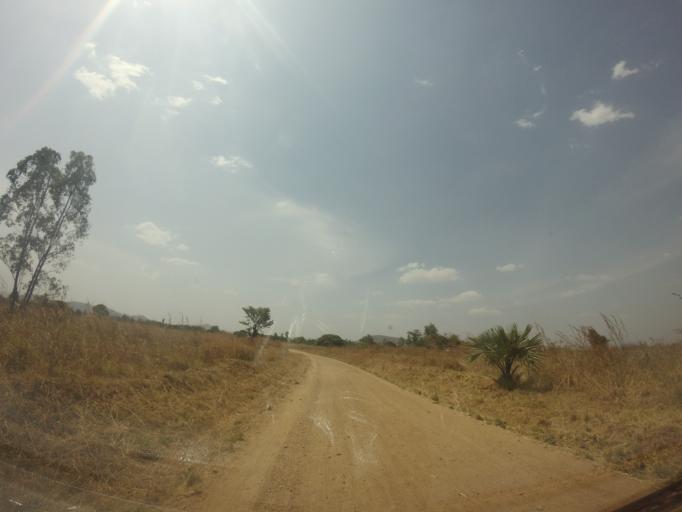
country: UG
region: Northern Region
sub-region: Arua District
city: Arua
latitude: 2.9116
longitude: 31.0496
